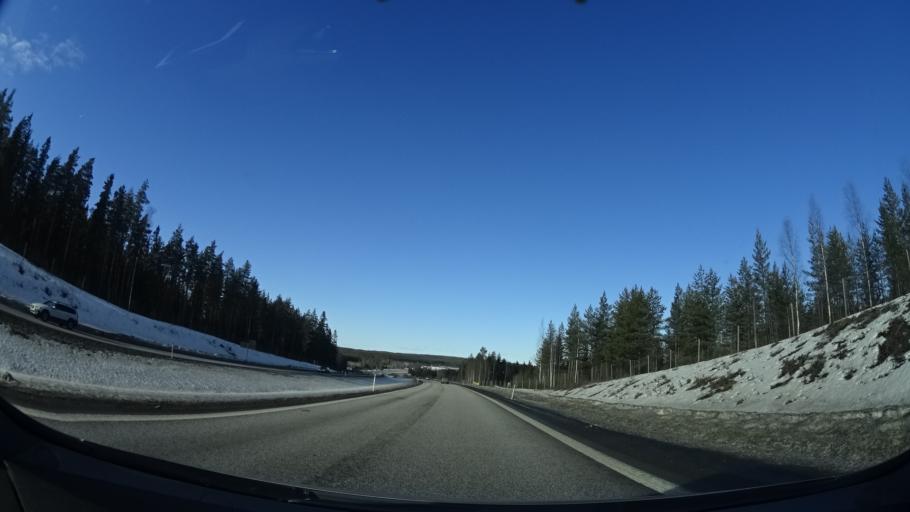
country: SE
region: Vaesterbotten
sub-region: Skelleftea Kommun
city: Kage
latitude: 64.7742
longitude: 21.0226
